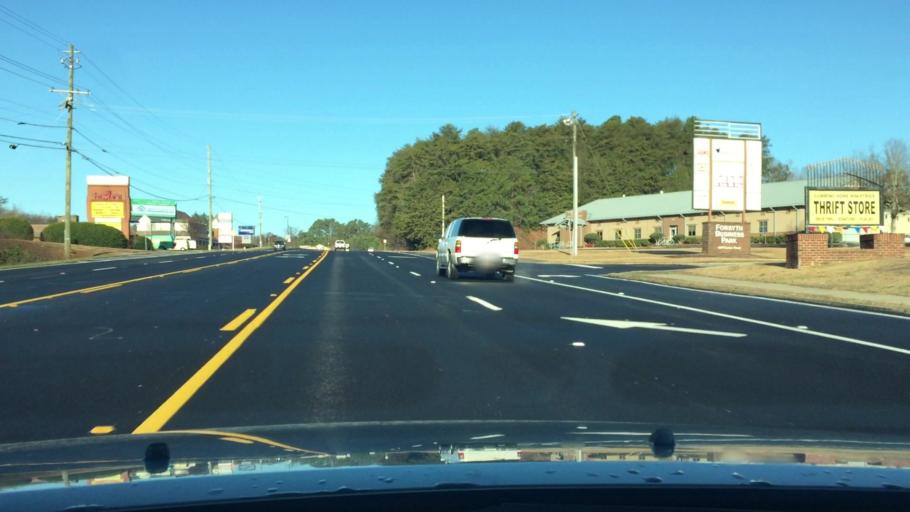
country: US
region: Georgia
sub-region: Forsyth County
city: Cumming
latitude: 34.2162
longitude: -84.1490
